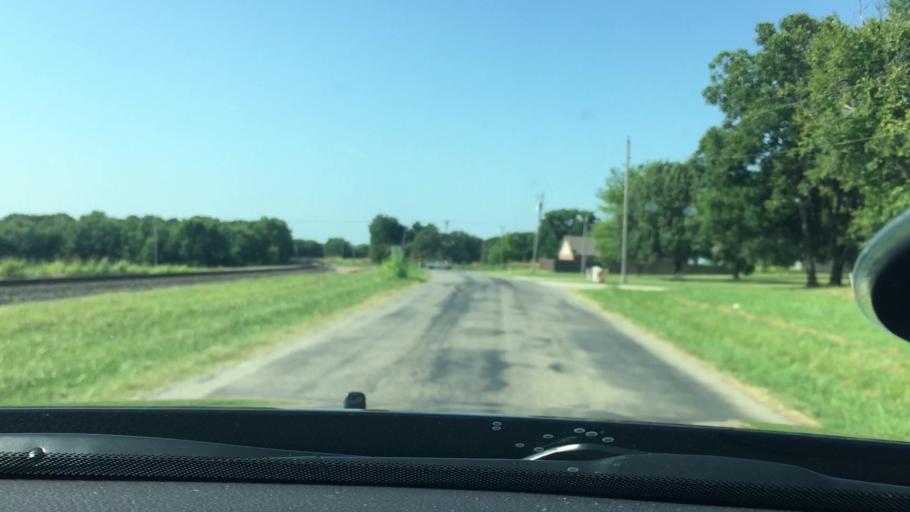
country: US
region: Oklahoma
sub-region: Pontotoc County
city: Byng
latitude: 34.8121
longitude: -96.6263
